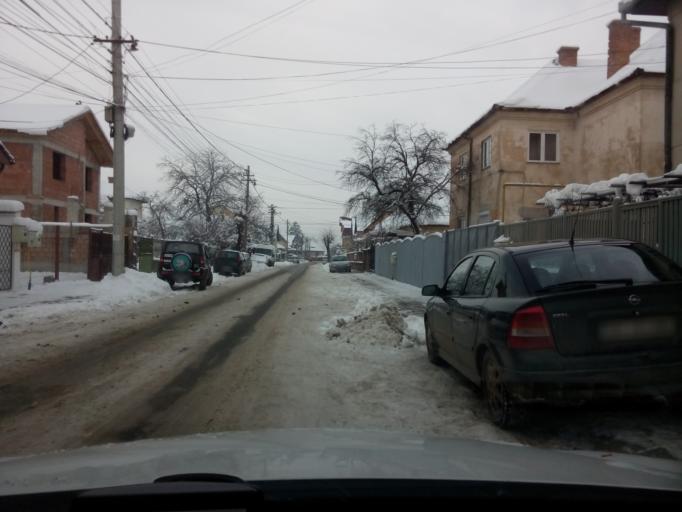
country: RO
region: Sibiu
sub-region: Municipiul Sibiu
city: Sibiu
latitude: 45.7878
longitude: 24.1665
